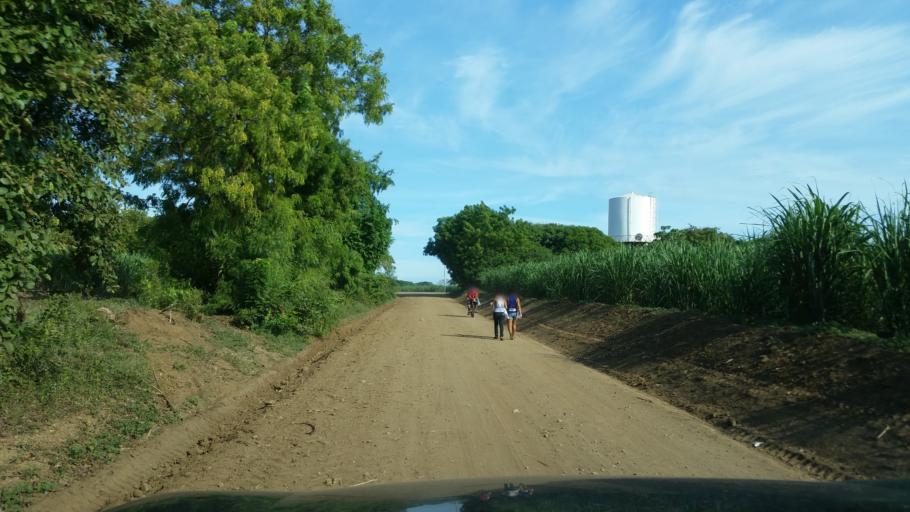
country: NI
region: Managua
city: Masachapa
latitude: 11.7937
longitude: -86.5051
